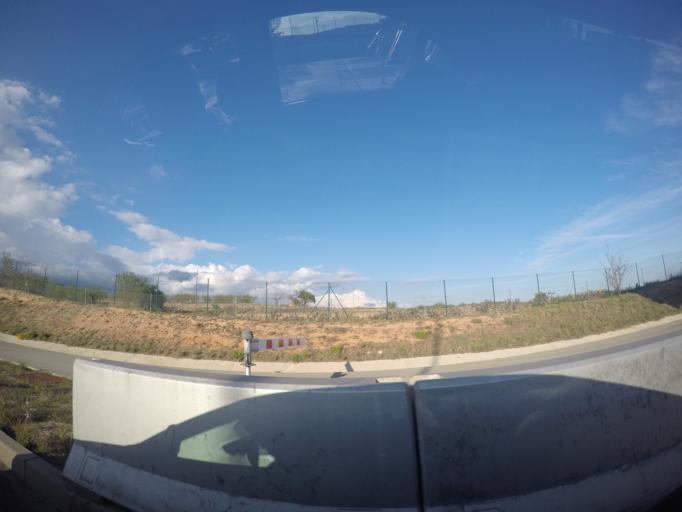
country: ES
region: Catalonia
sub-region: Provincia de Tarragona
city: la Bisbal del Penedes
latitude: 41.2805
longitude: 1.4982
